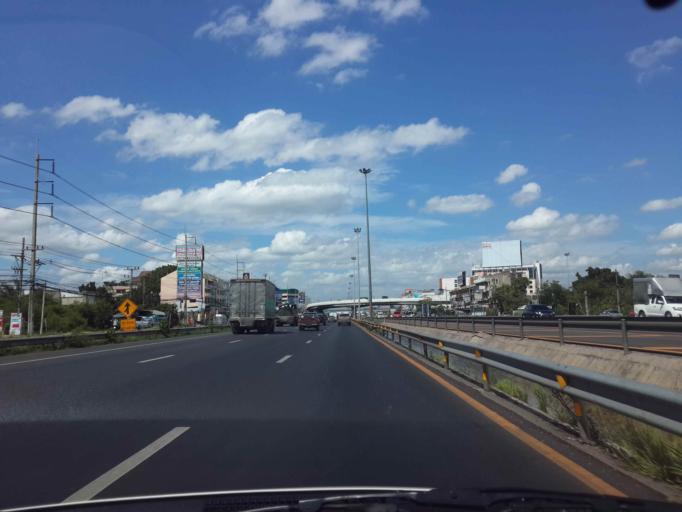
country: TH
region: Samut Sakhon
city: Samut Sakhon
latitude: 13.5546
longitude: 100.2681
